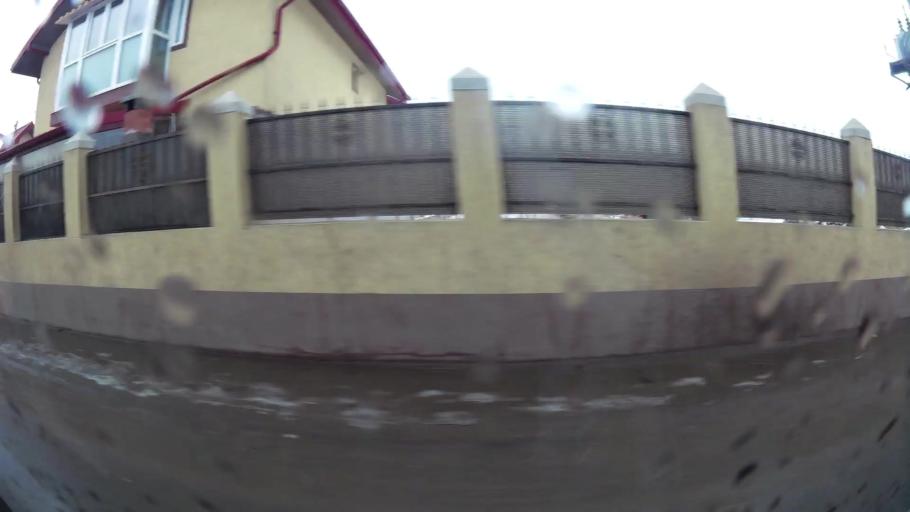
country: RO
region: Ilfov
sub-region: Comuna Bragadiru
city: Bragadiru
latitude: 44.4018
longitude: 26.0103
